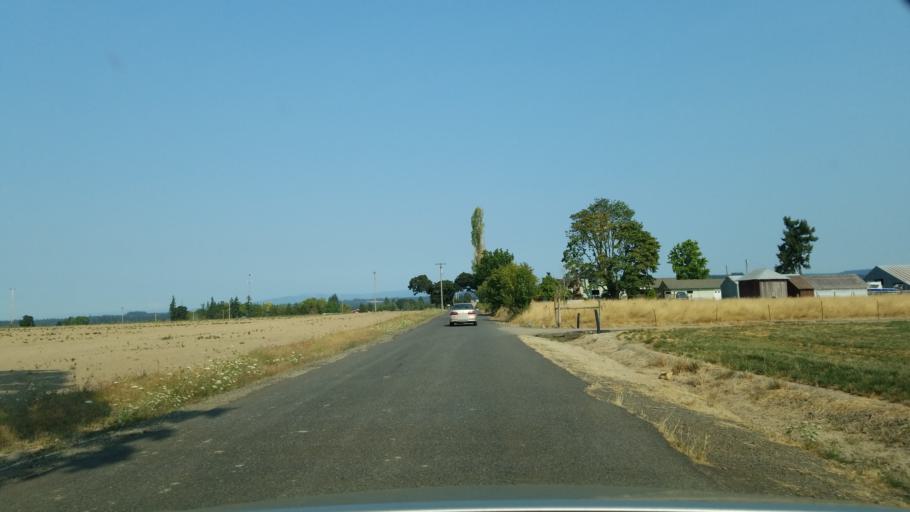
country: US
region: Oregon
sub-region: Marion County
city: Mount Angel
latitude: 45.0711
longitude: -122.7021
